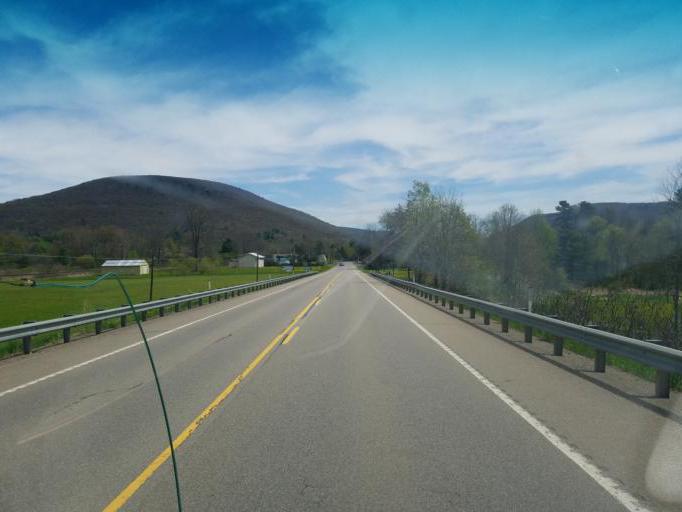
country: US
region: Pennsylvania
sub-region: Potter County
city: Galeton
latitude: 41.7437
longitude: -77.6073
